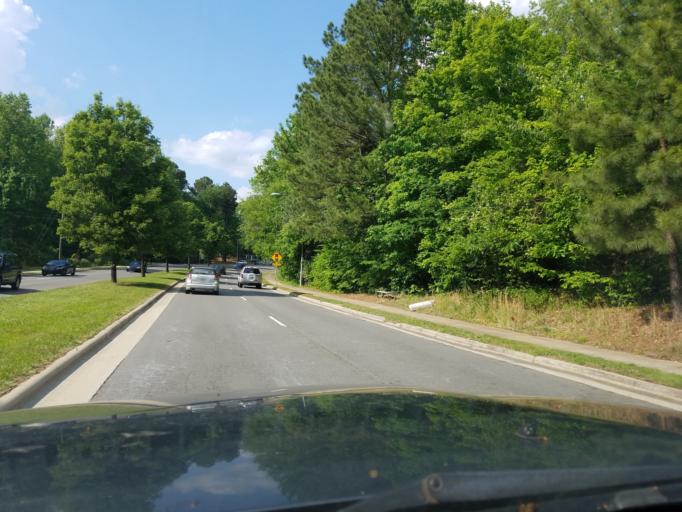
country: US
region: North Carolina
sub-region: Durham County
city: Durham
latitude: 35.9569
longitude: -78.9661
